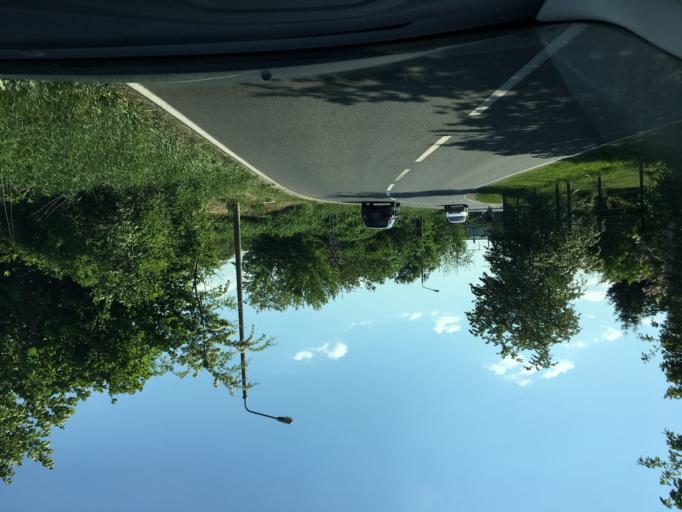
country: DE
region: Saxony
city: Taucha
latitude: 51.3667
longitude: 12.4448
